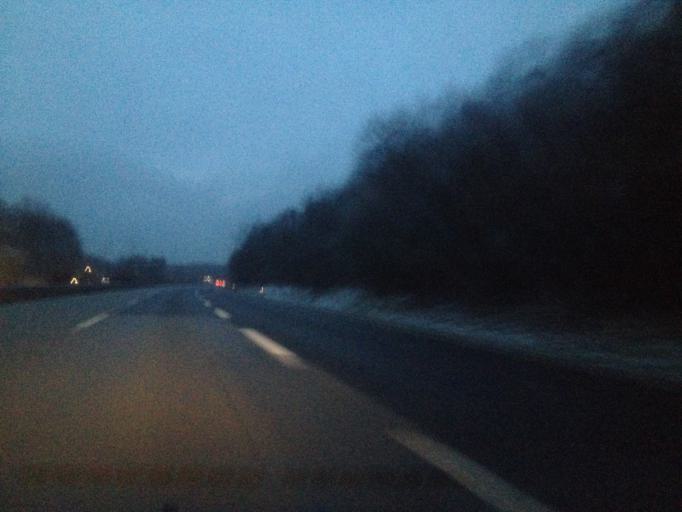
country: DE
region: Rheinland-Pfalz
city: Bad Neuenahr-Ahrweiler
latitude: 50.5742
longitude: 7.1303
